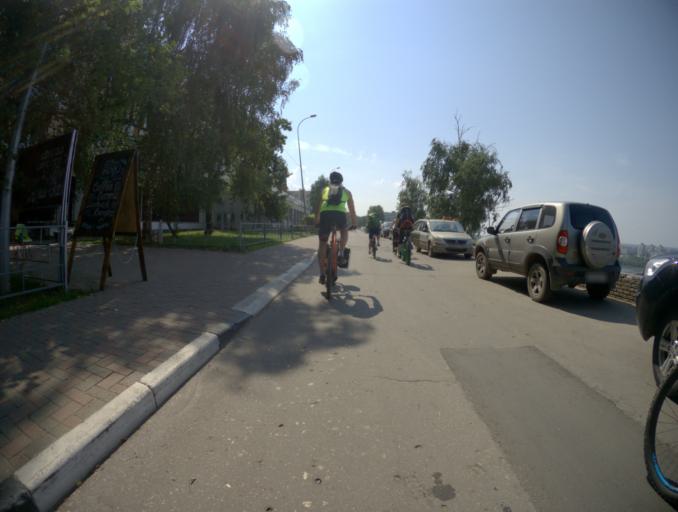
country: RU
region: Nizjnij Novgorod
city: Nizhniy Novgorod
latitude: 56.3259
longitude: 43.9866
